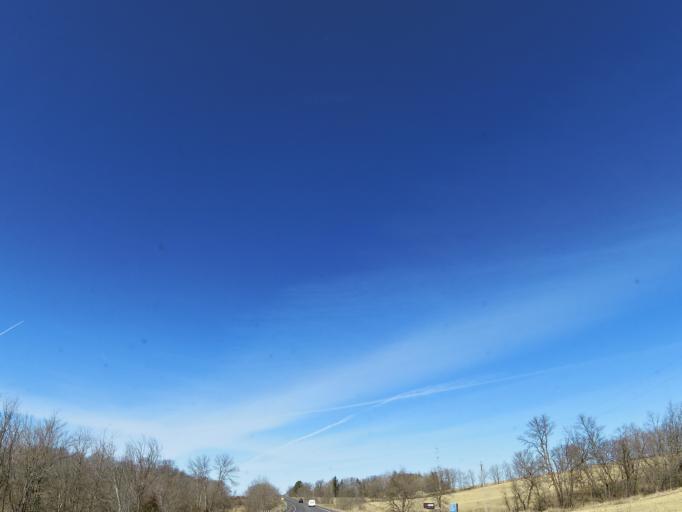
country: US
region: Minnesota
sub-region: Wright County
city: Rockford
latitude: 45.1092
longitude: -93.7822
